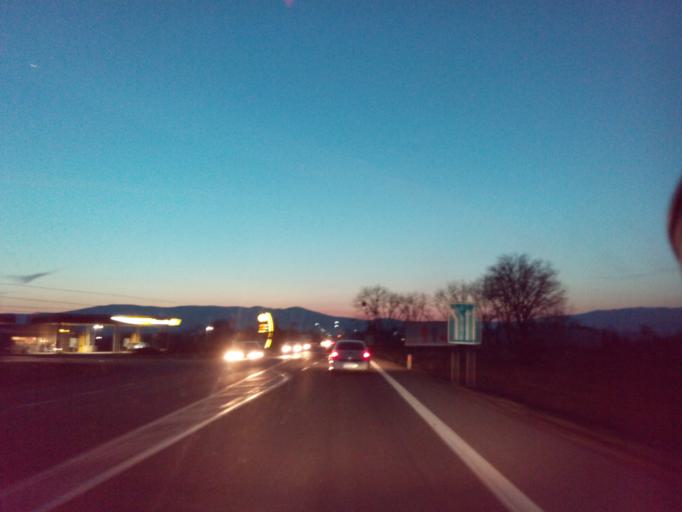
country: SK
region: Kosicky
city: Secovce
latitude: 48.7022
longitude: 21.6877
